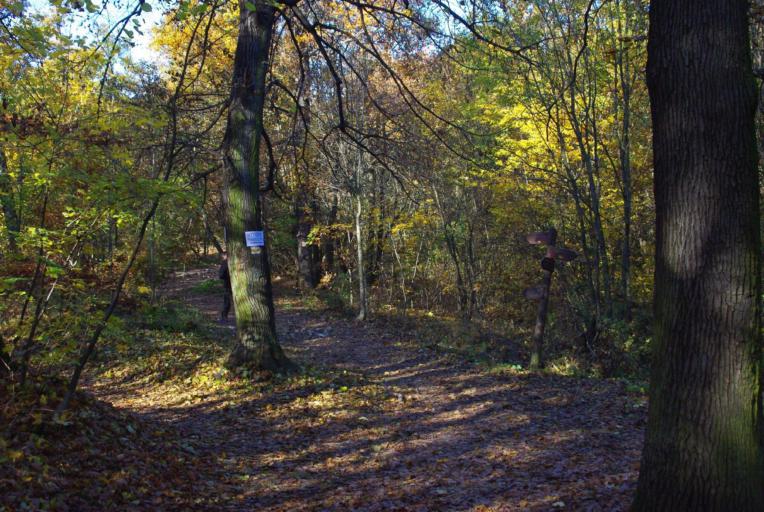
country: HU
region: Pest
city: Budakeszi
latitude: 47.5303
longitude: 18.9648
